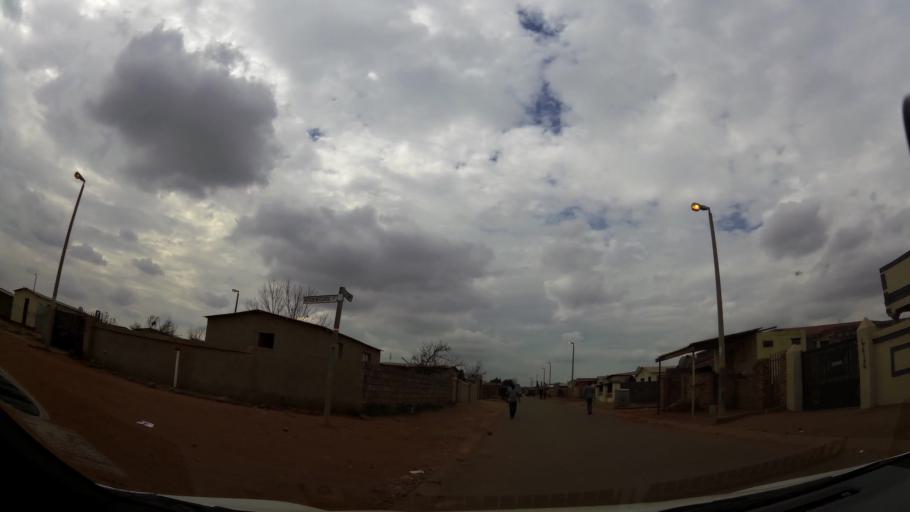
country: ZA
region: Gauteng
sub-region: Ekurhuleni Metropolitan Municipality
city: Germiston
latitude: -26.3821
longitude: 28.1202
